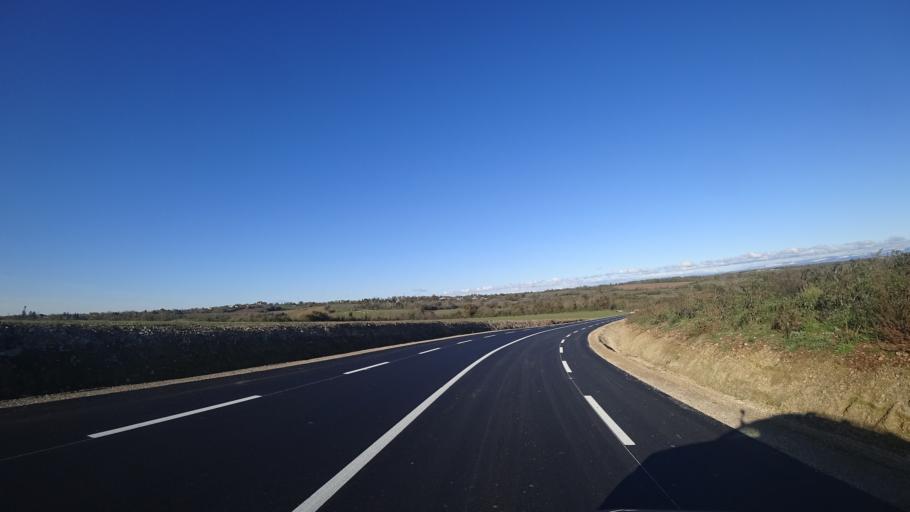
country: FR
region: Midi-Pyrenees
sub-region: Departement de l'Aveyron
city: Olemps
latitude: 44.3773
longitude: 2.5519
